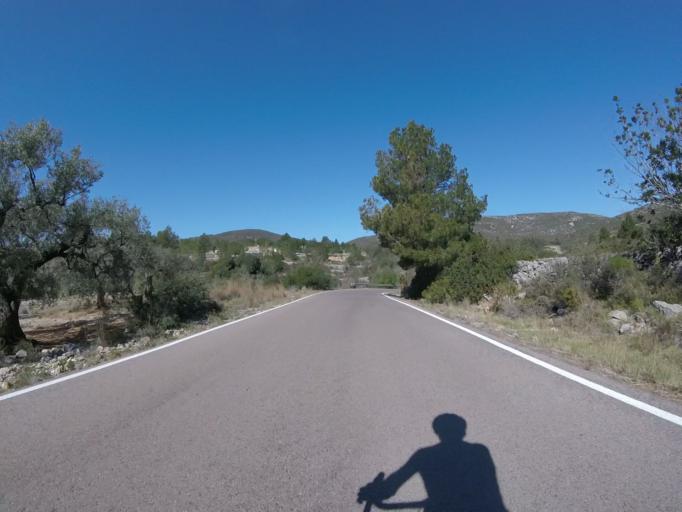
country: ES
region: Valencia
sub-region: Provincia de Castello
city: Santa Magdalena de Pulpis
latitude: 40.3785
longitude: 0.2692
